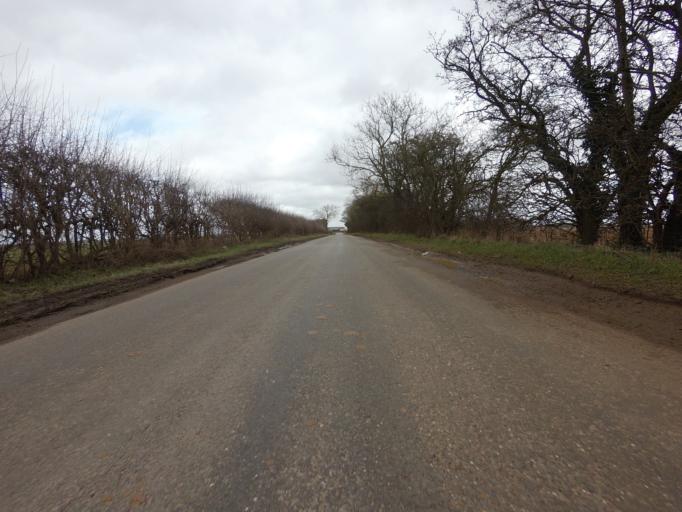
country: GB
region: England
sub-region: Lincolnshire
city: Grantham
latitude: 52.8806
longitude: -0.6651
